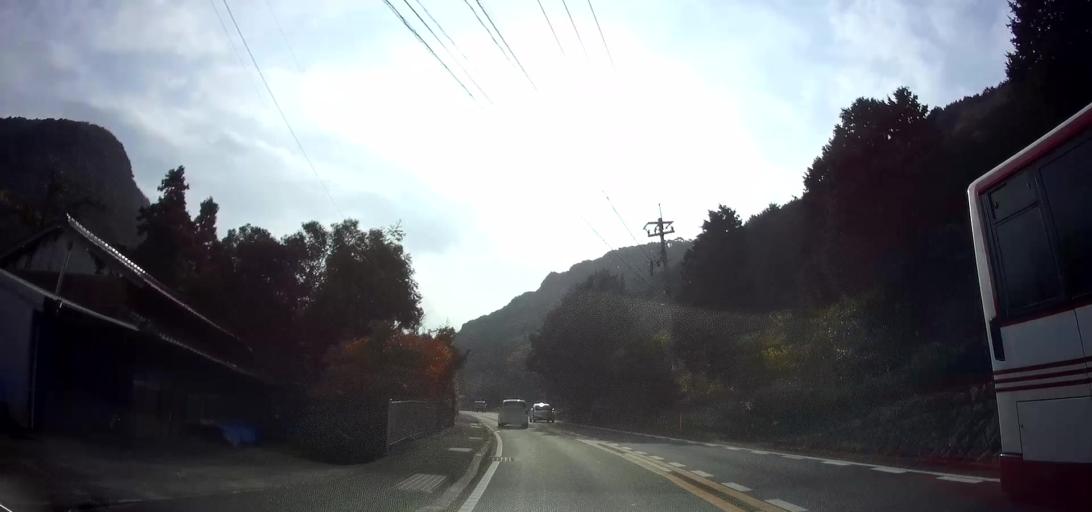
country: JP
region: Nagasaki
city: Shimabara
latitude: 32.7774
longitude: 130.2107
